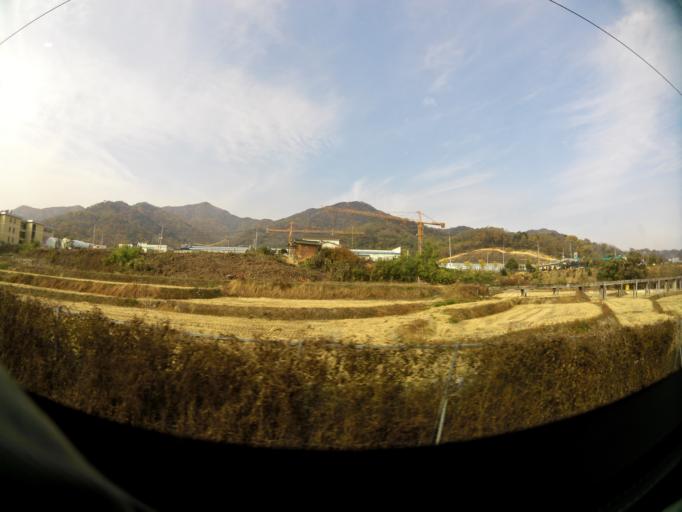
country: KR
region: Gyeongsangbuk-do
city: Gumi
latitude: 36.0916
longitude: 128.3529
